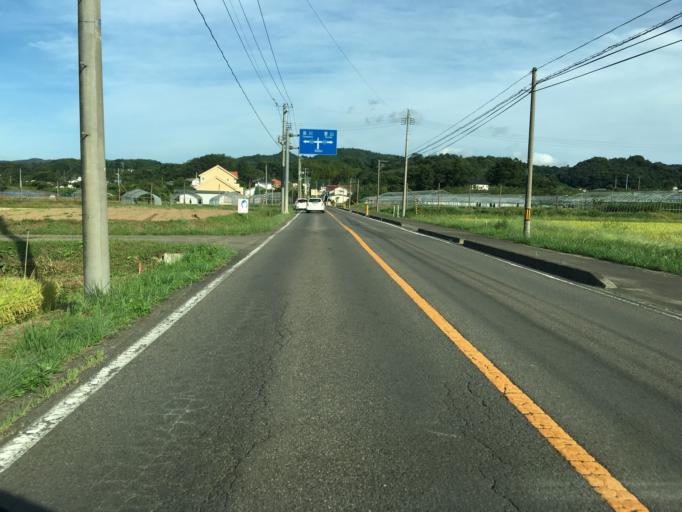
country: JP
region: Fukushima
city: Hobaramachi
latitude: 37.8196
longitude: 140.5838
